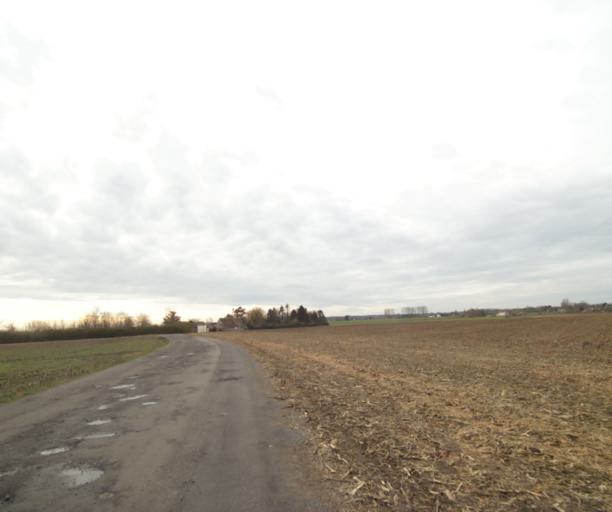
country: FR
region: Nord-Pas-de-Calais
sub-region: Departement du Nord
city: Hergnies
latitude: 50.4827
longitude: 3.5484
